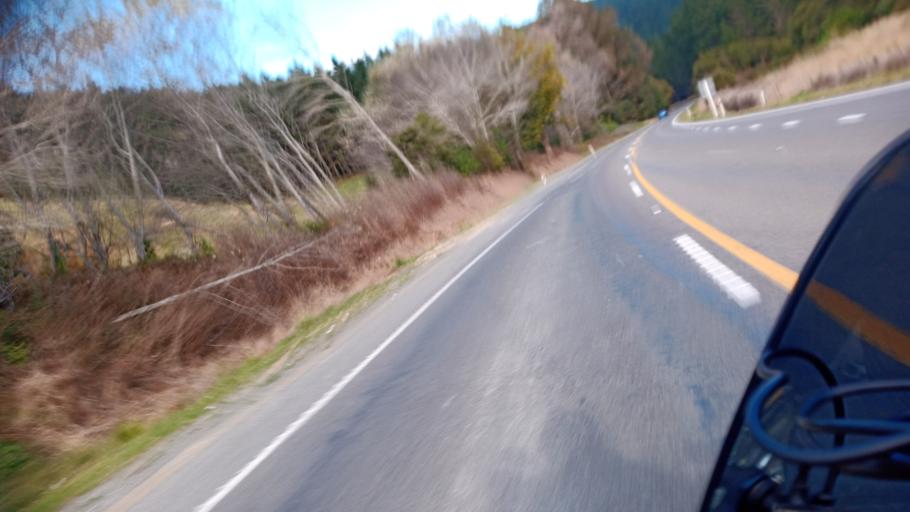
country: NZ
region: Gisborne
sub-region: Gisborne District
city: Gisborne
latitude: -38.8294
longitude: 177.9011
